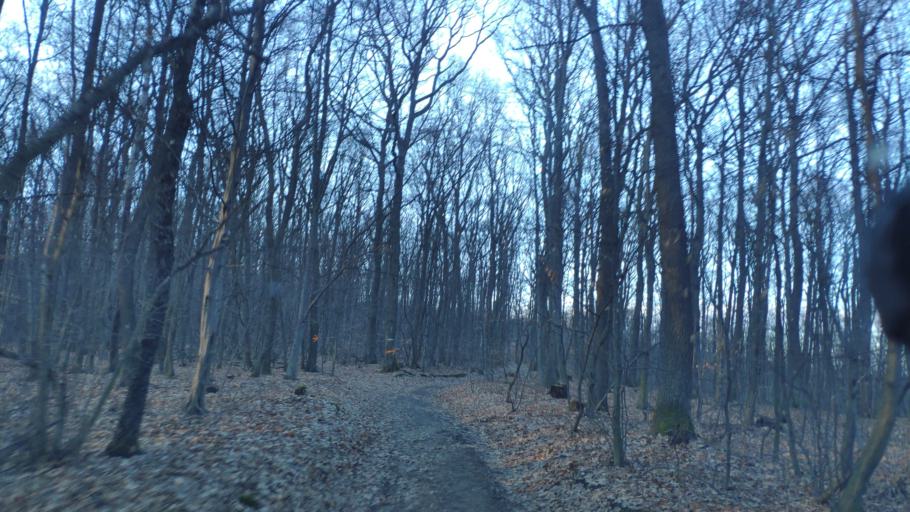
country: SK
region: Kosicky
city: Kosice
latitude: 48.6918
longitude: 21.1815
